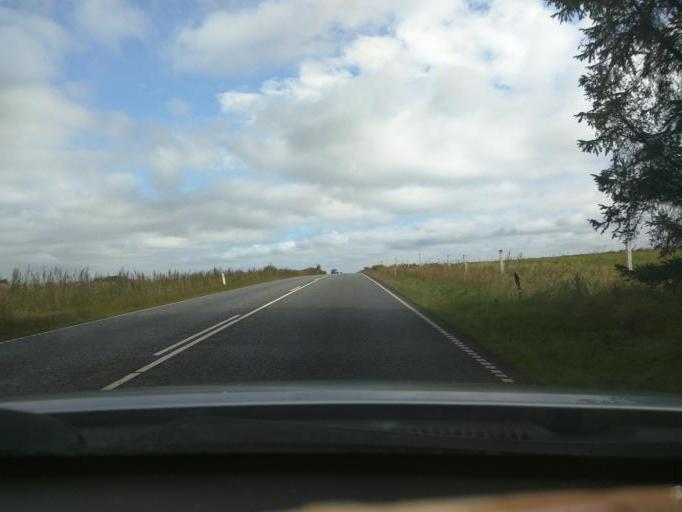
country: DK
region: Central Jutland
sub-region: Viborg Kommune
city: Viborg
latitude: 56.3666
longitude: 9.3711
